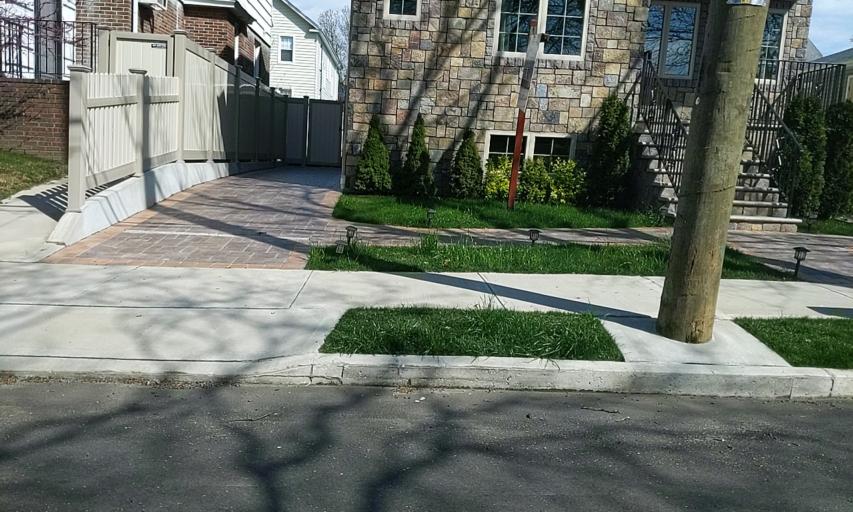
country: US
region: New York
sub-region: Richmond County
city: Bloomfield
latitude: 40.6202
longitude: -74.1388
